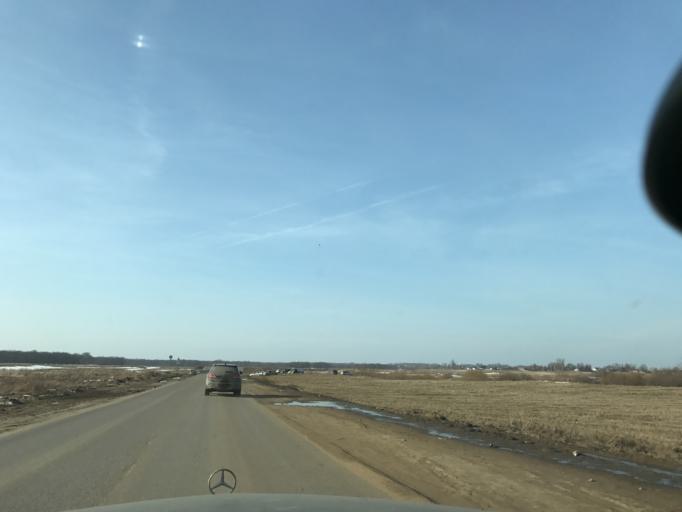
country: RU
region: Nizjnij Novgorod
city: Pavlovo
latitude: 55.9726
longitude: 43.0612
